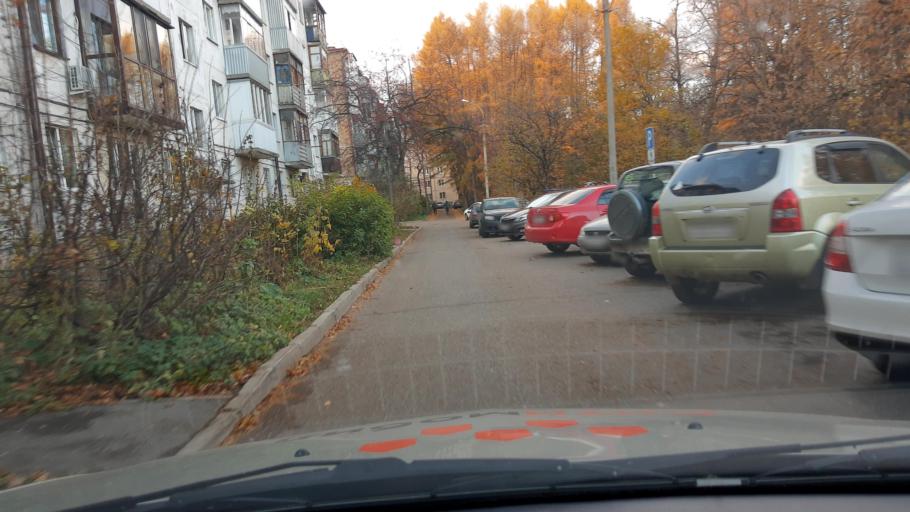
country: RU
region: Bashkortostan
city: Ufa
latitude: 54.7931
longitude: 56.0474
